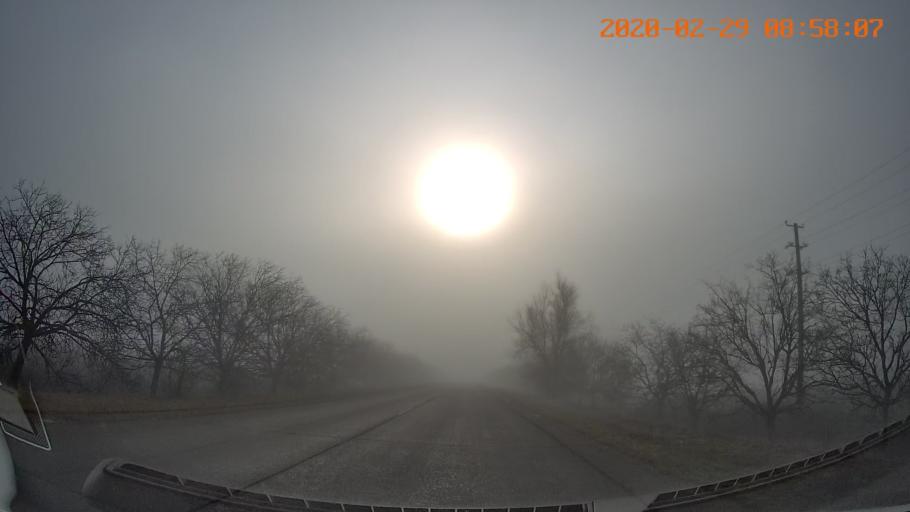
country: MD
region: Telenesti
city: Tiraspolul Nou
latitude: 46.9232
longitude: 29.6361
